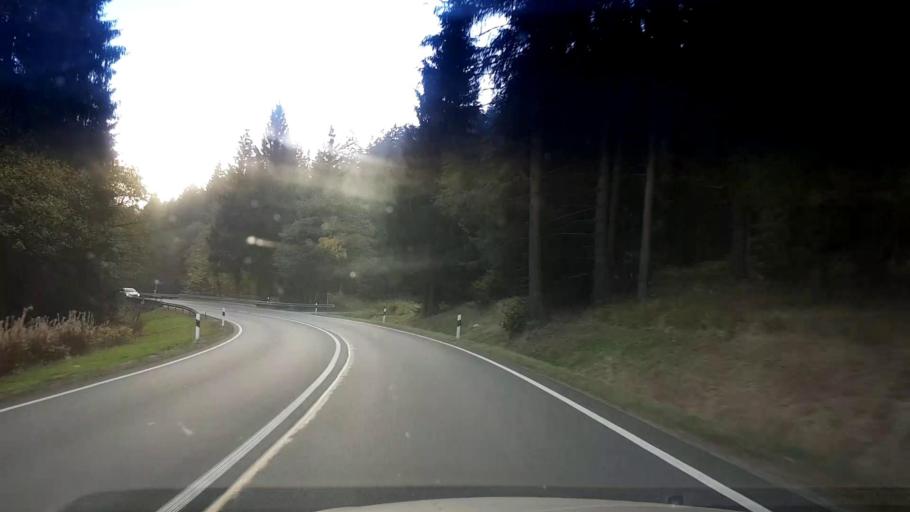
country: DE
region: Bavaria
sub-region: Upper Franconia
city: Bischofsgrun
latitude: 50.0607
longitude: 11.7857
